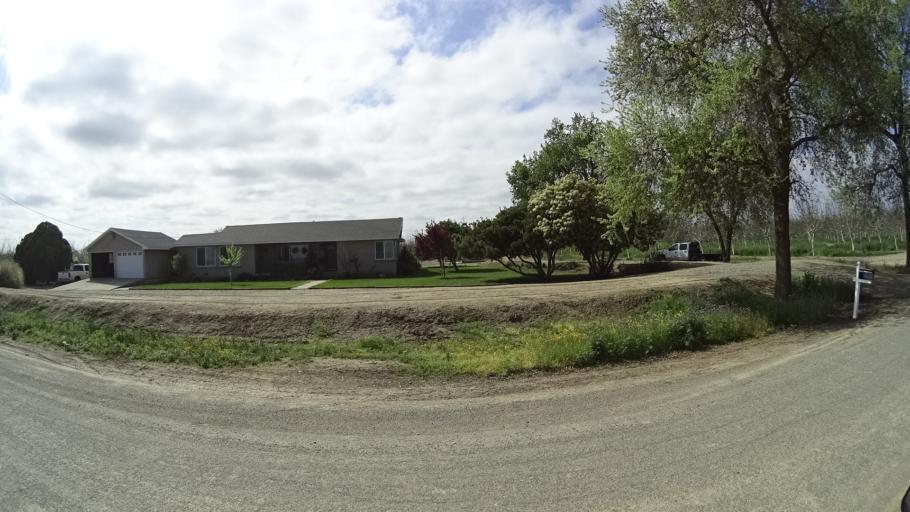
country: US
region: California
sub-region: Colusa County
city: Colusa
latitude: 39.4199
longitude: -121.9535
